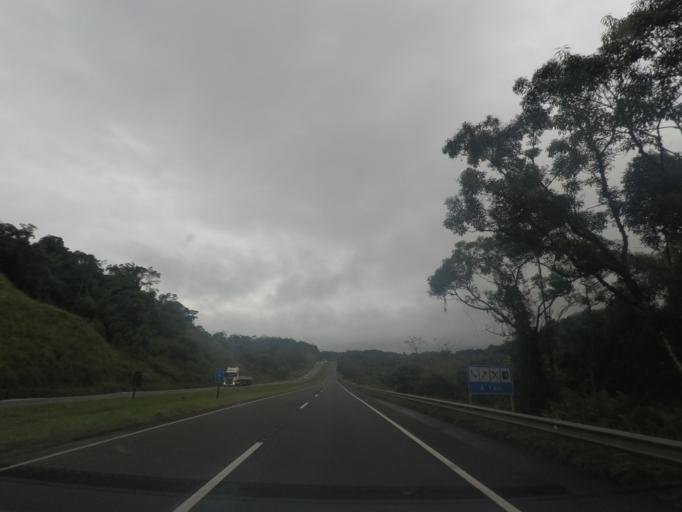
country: BR
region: Parana
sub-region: Antonina
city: Antonina
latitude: -25.0910
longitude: -48.6475
